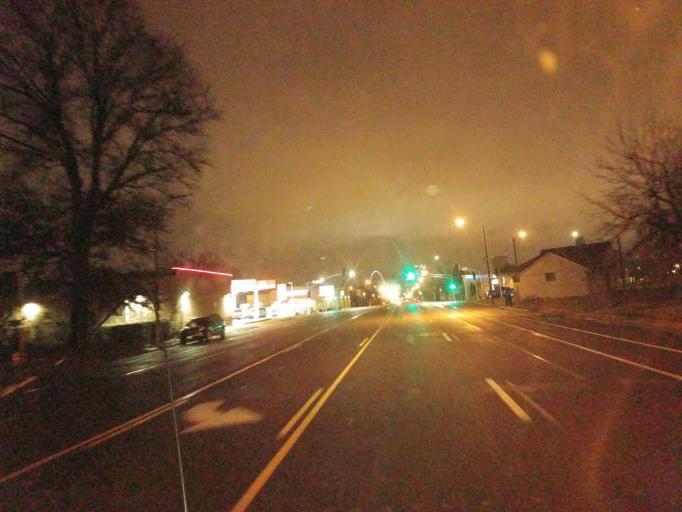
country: US
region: Missouri
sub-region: City of Saint Louis
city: St. Louis
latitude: 38.6514
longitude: -90.2004
